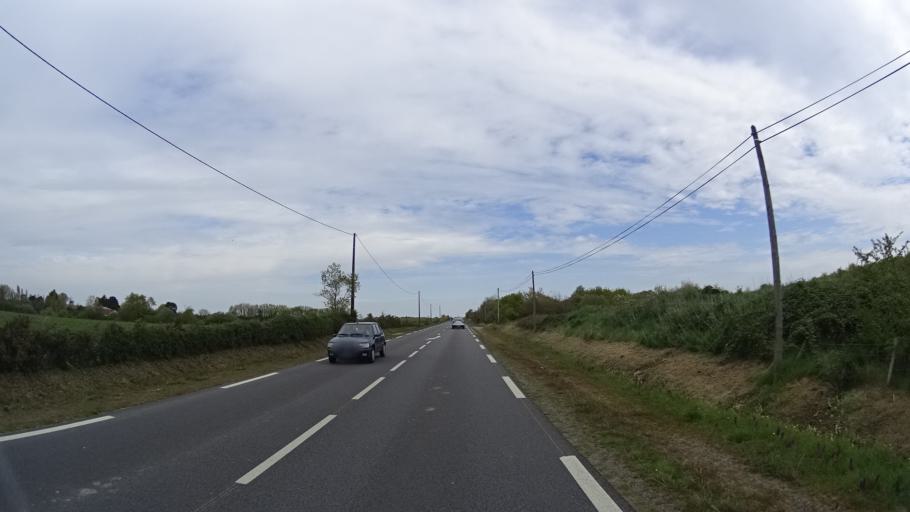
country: FR
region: Pays de la Loire
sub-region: Departement de la Loire-Atlantique
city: Bourgneuf-en-Retz
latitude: 47.0474
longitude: -1.9374
